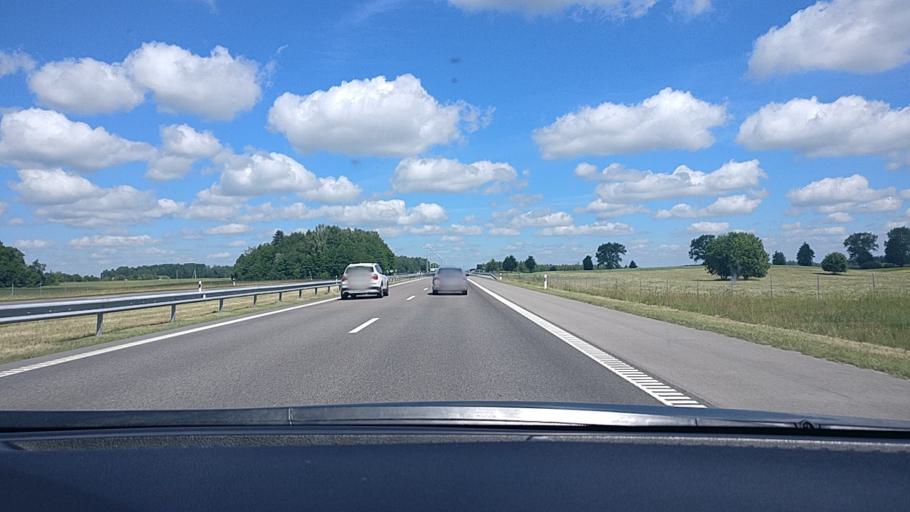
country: LT
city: Sirvintos
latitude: 55.1143
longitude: 24.8471
